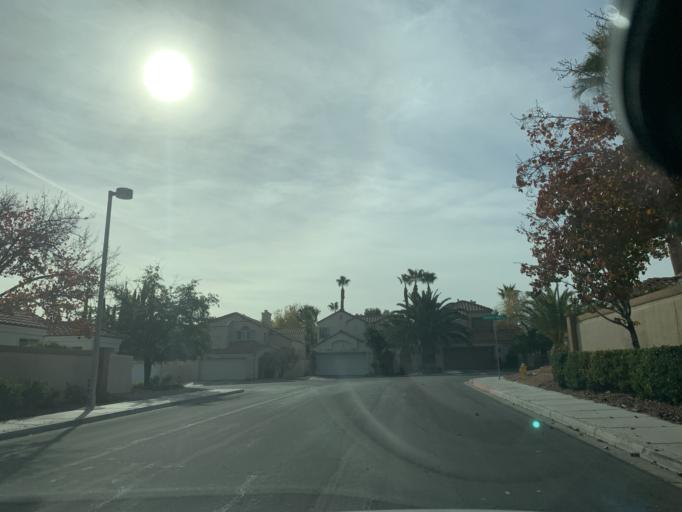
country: US
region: Nevada
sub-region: Clark County
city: Summerlin South
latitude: 36.1516
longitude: -115.2965
